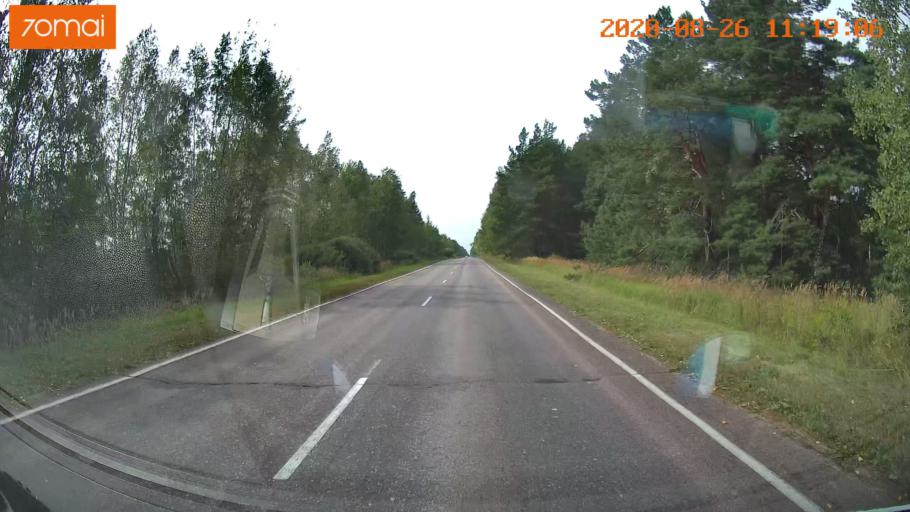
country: RU
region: Rjazan
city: Shilovo
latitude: 54.4029
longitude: 41.0855
